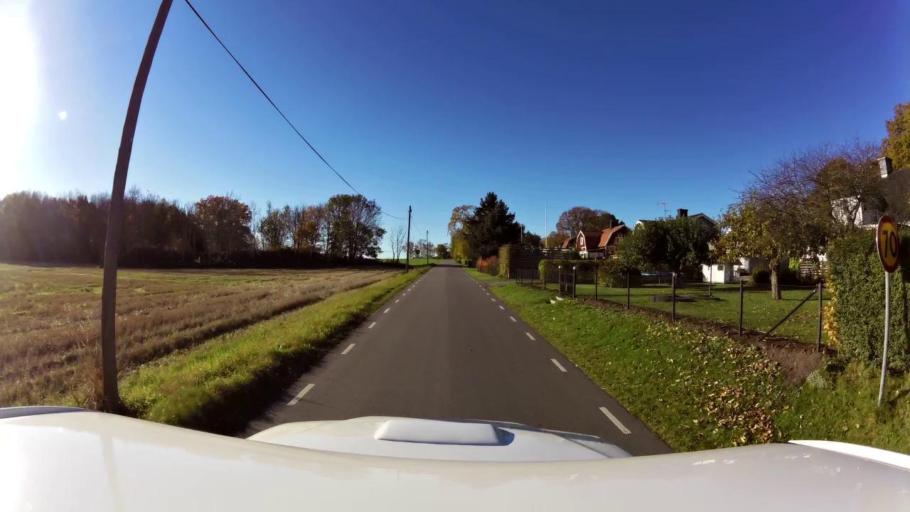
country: SE
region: OEstergoetland
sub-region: Linkopings Kommun
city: Ljungsbro
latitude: 58.5196
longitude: 15.4226
